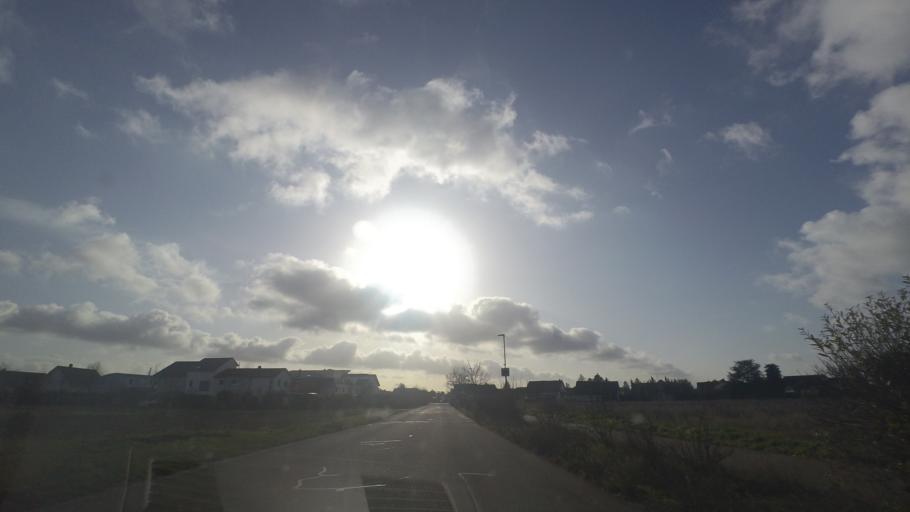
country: DE
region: Baden-Wuerttemberg
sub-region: Karlsruhe Region
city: Karlsdorf-Neuthard
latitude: 49.1200
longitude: 8.5108
